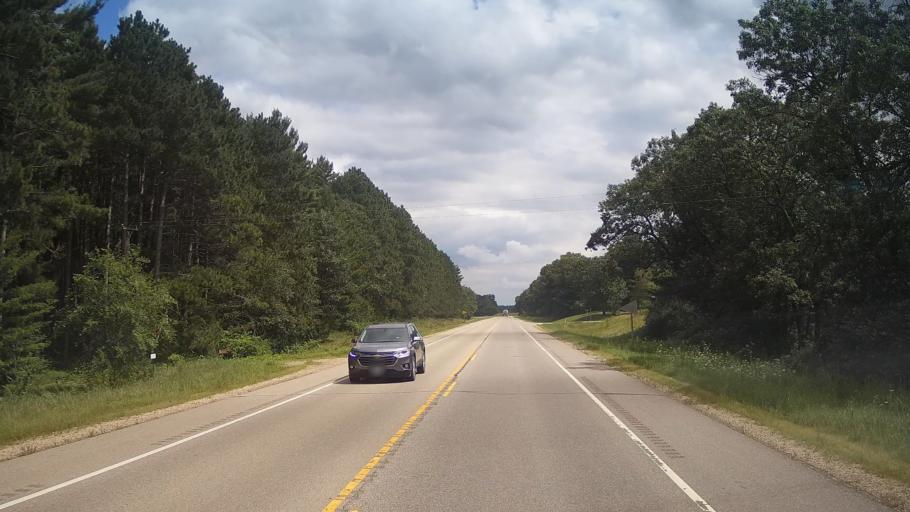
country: US
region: Wisconsin
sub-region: Marquette County
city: Westfield
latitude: 44.0218
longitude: -89.5529
